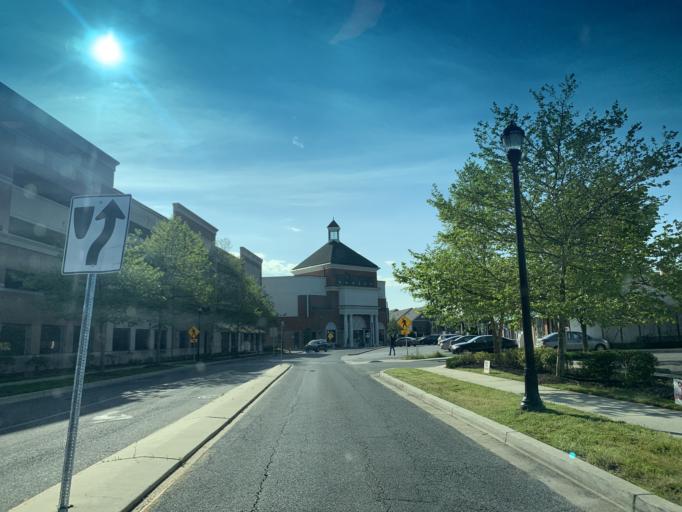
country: US
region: Maryland
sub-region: Anne Arundel County
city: Parole
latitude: 38.9818
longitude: -76.5384
